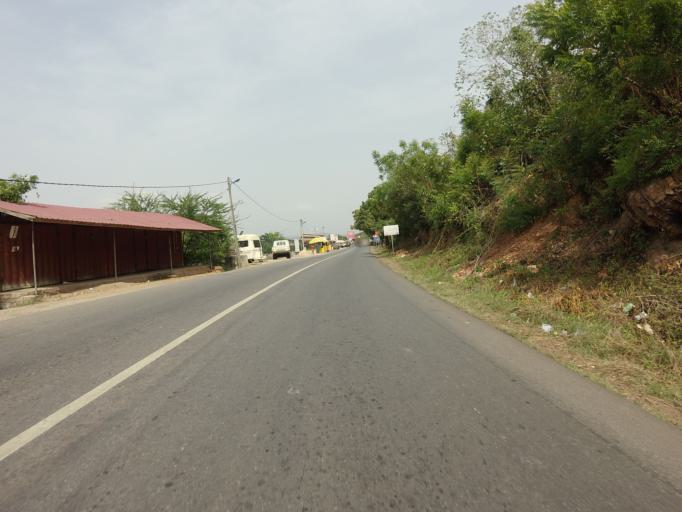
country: GH
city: Akropong
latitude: 6.2386
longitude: 0.0986
